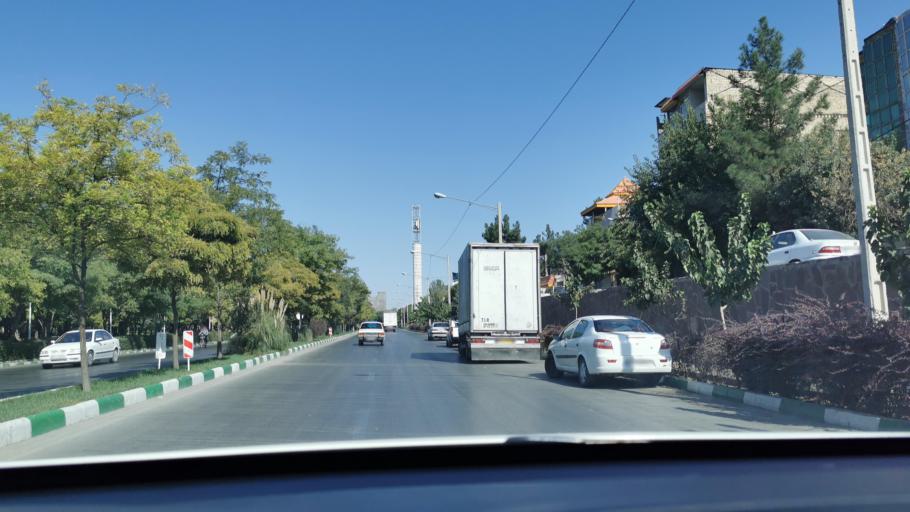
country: IR
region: Razavi Khorasan
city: Mashhad
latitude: 36.3331
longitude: 59.6374
